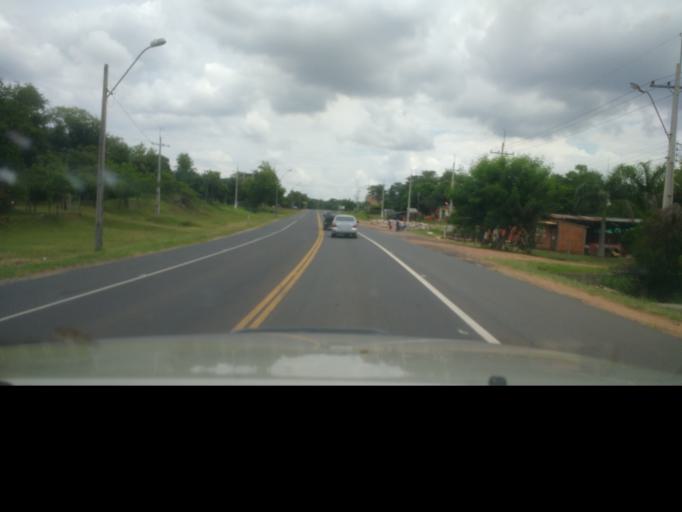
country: PY
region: Central
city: Limpio
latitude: -25.1318
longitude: -57.4471
